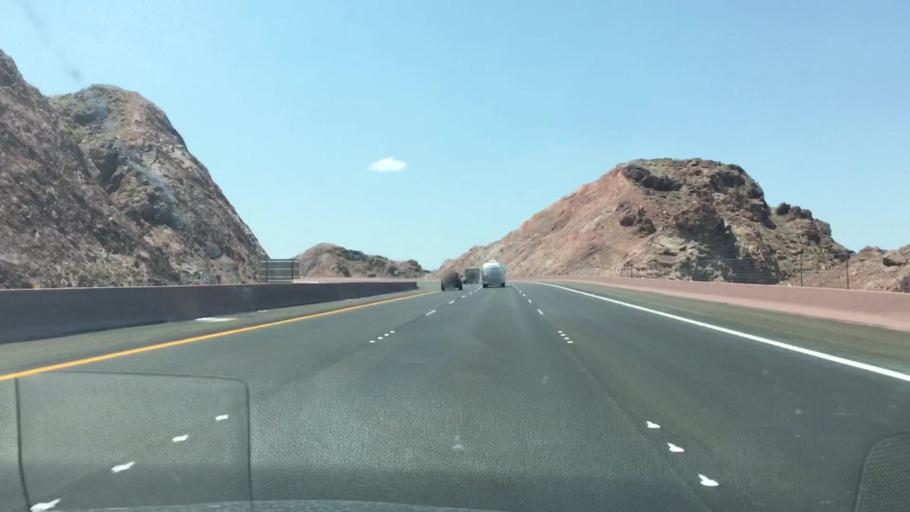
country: US
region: Nevada
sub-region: Clark County
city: Boulder City
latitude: 36.0033
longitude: -114.7900
